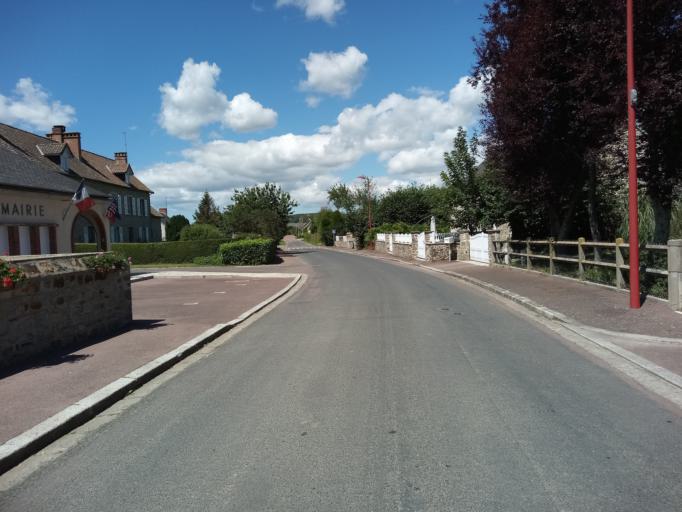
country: FR
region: Lower Normandy
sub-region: Departement de la Manche
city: Periers
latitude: 49.2809
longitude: -1.4255
